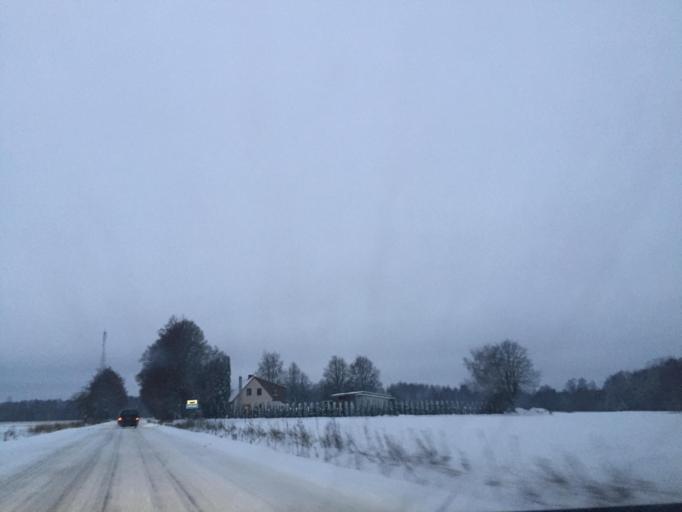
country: LV
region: Raunas
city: Rauna
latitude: 57.4254
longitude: 25.5925
